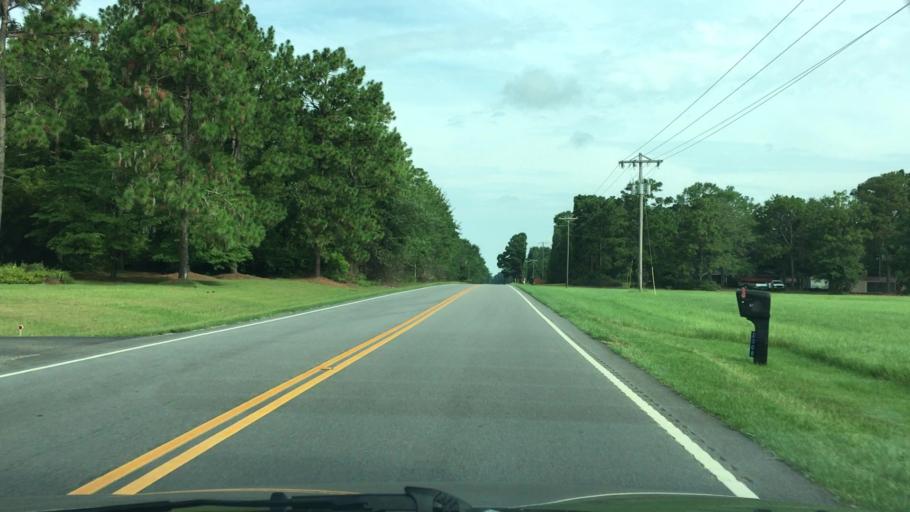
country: US
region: South Carolina
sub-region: Lexington County
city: Batesburg-Leesville
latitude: 33.7135
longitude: -81.4974
